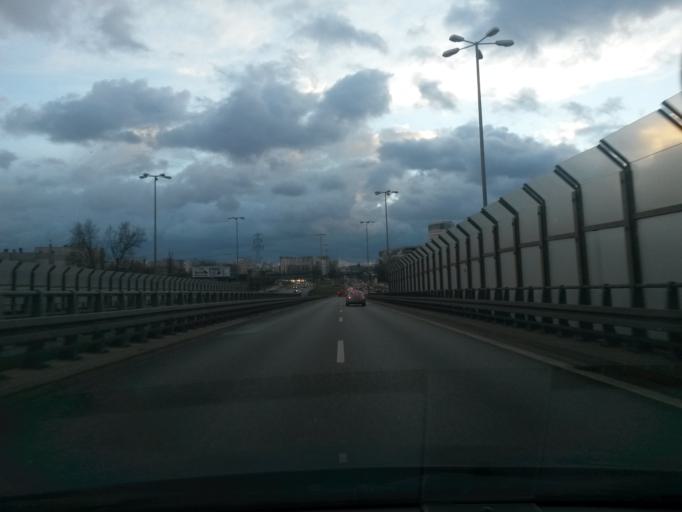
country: PL
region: Masovian Voivodeship
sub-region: Warszawa
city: Mokotow
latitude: 52.1946
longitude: 21.0492
